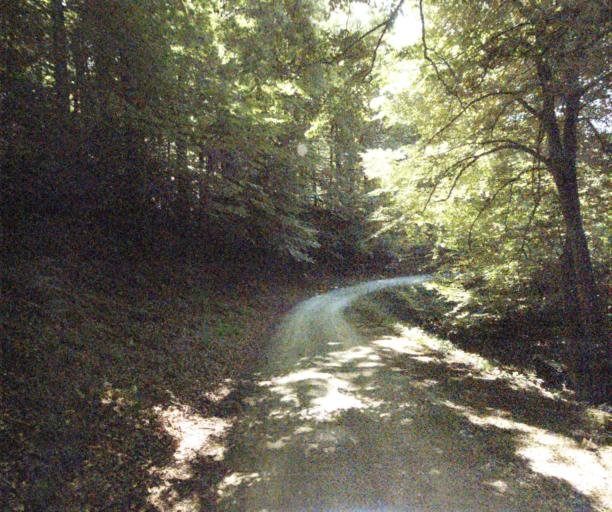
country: FR
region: Midi-Pyrenees
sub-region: Departement du Tarn
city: Soreze
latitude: 43.4383
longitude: 2.0926
